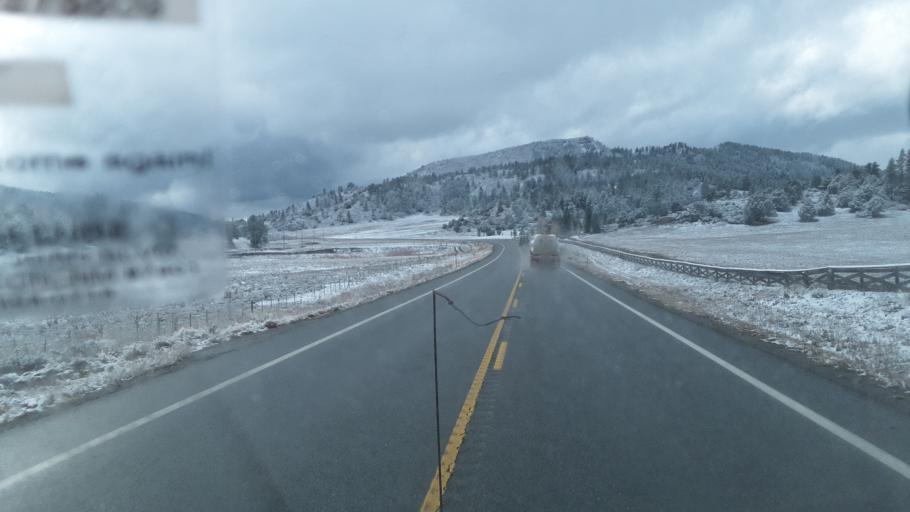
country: US
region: Colorado
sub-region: Archuleta County
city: Pagosa Springs
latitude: 37.2285
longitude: -107.2088
